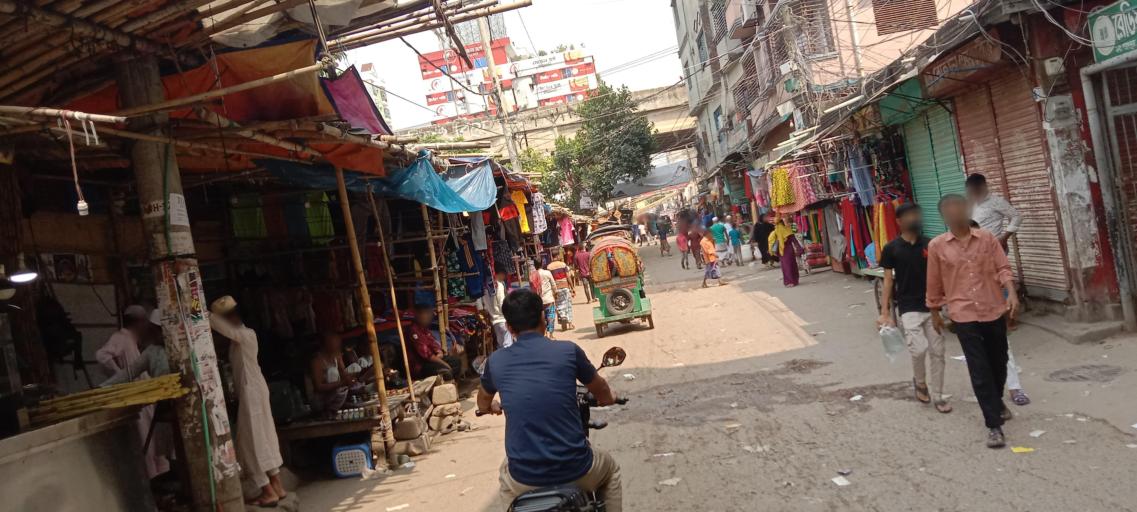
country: BD
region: Dhaka
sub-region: Dhaka
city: Dhaka
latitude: 23.7068
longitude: 90.3995
